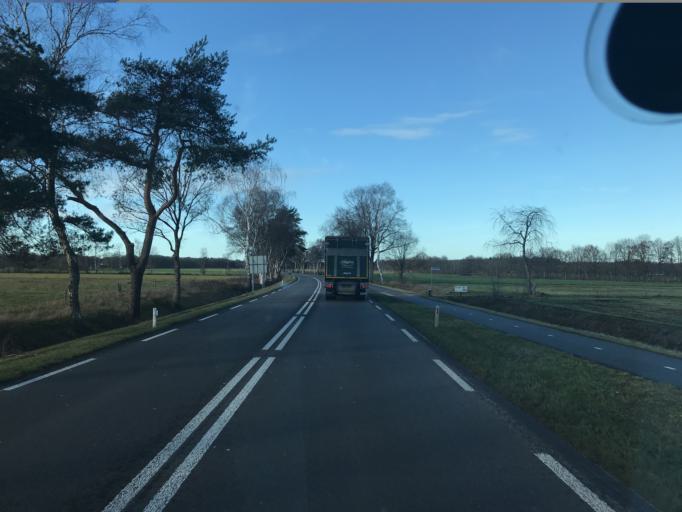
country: NL
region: Gelderland
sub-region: Gemeente Barneveld
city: Garderen
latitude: 52.2755
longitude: 5.7257
